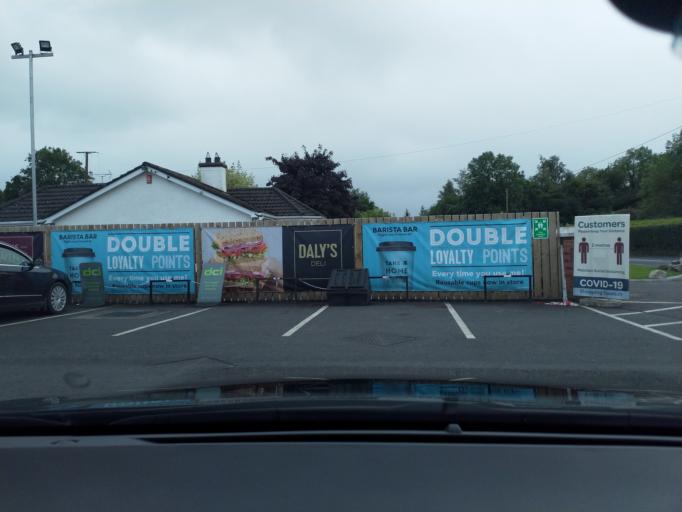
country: GB
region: Northern Ireland
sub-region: Dungannon District
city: Dungannon
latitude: 54.4454
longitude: -6.7951
